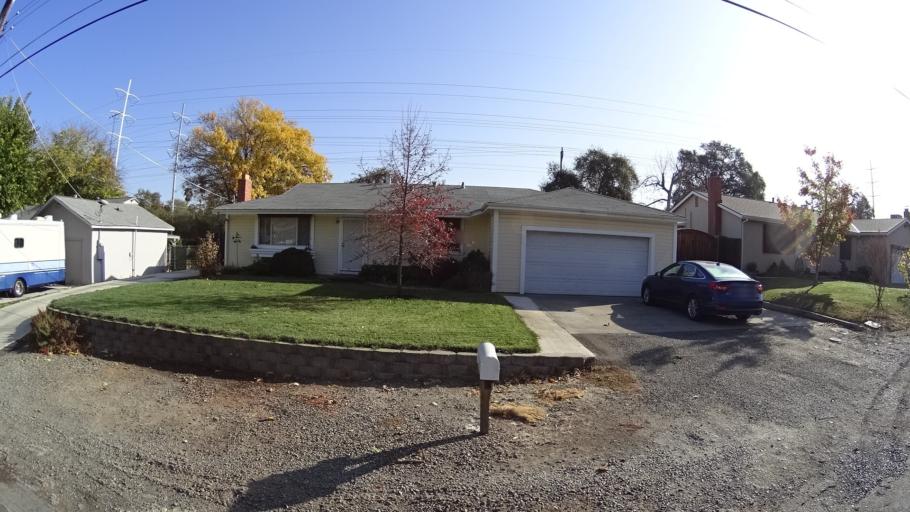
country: US
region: California
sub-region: Sacramento County
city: Citrus Heights
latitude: 38.6996
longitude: -121.2542
